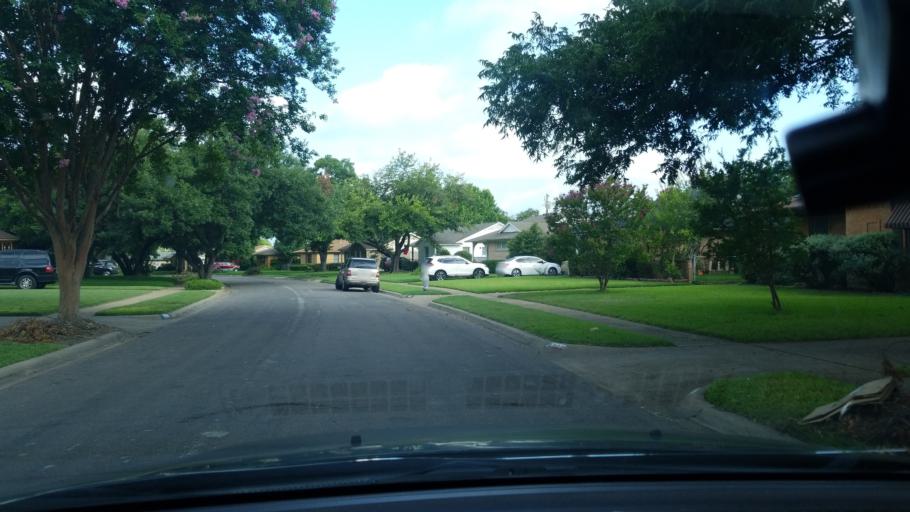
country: US
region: Texas
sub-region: Dallas County
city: Mesquite
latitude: 32.8204
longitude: -96.6824
